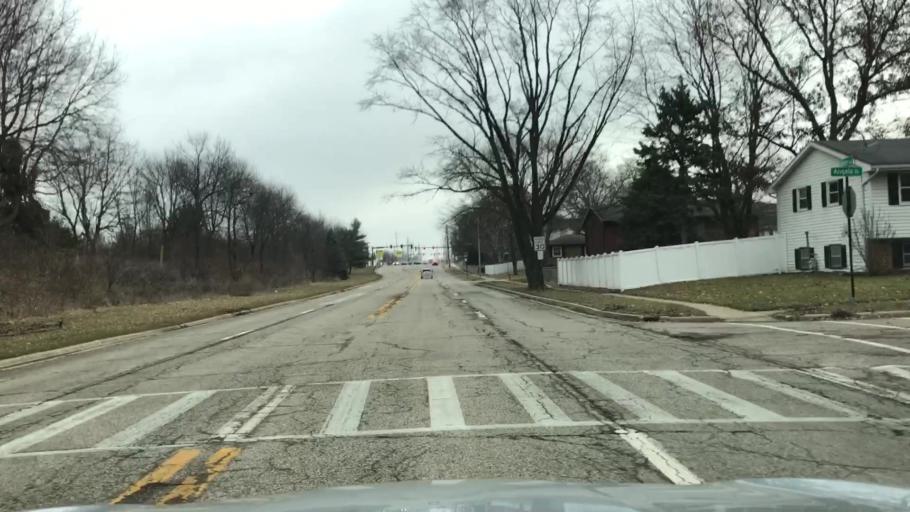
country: US
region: Illinois
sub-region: McLean County
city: Normal
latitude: 40.5026
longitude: -88.9612
